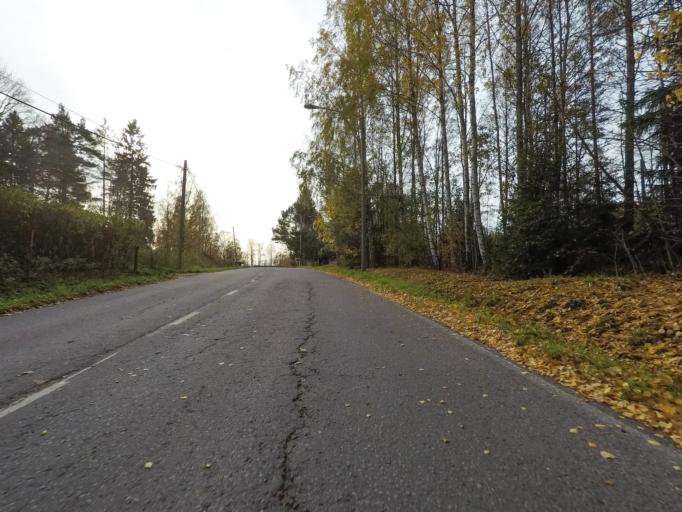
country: FI
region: Uusimaa
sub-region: Helsinki
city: Vantaa
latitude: 60.2573
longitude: 25.1425
